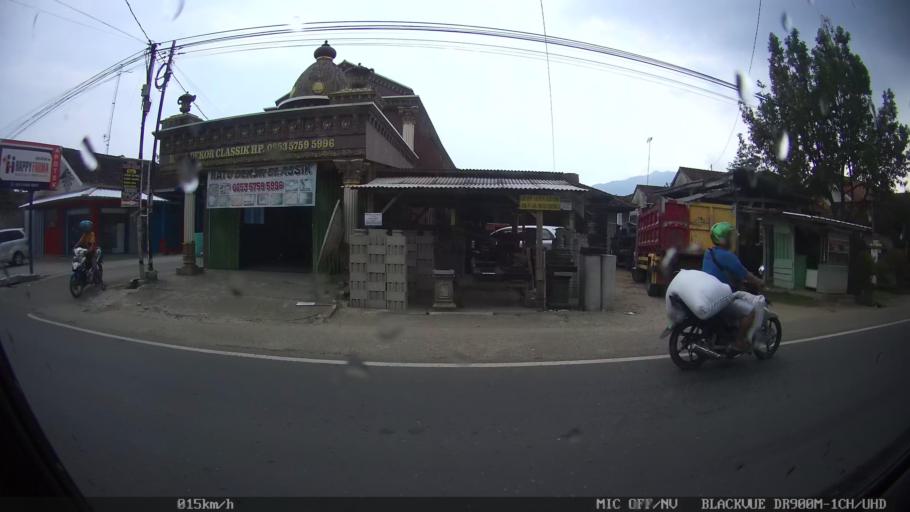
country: ID
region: Lampung
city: Gedongtataan
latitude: -5.3764
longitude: 105.1279
